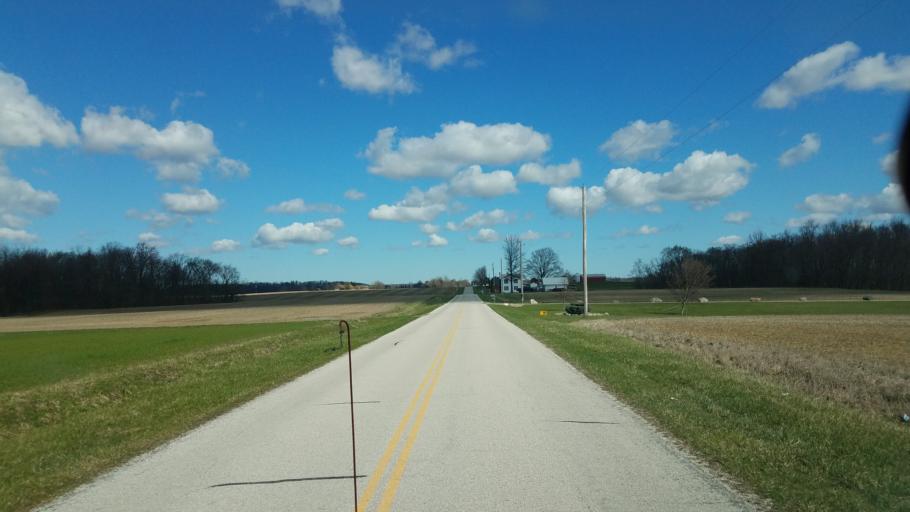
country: US
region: Ohio
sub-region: Sandusky County
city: Mount Carmel
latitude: 41.1507
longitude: -82.9382
